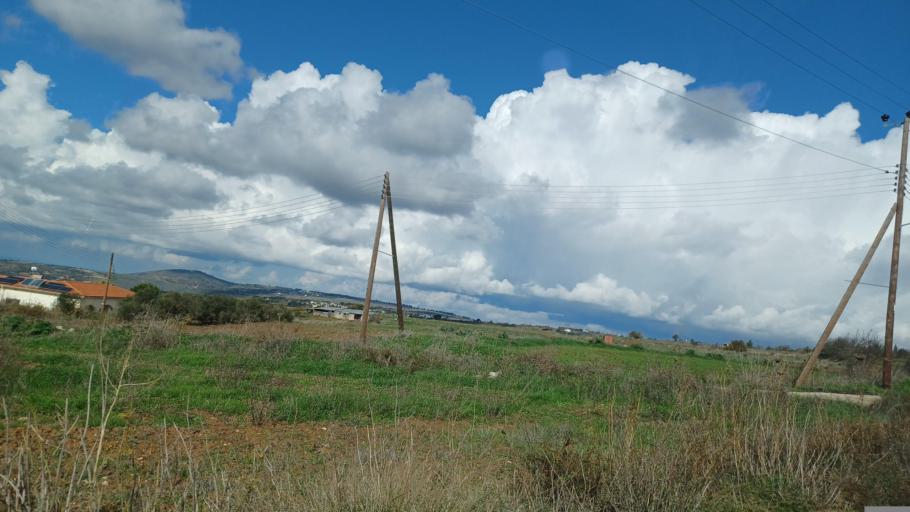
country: CY
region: Pafos
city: Pegeia
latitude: 34.9142
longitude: 32.4182
